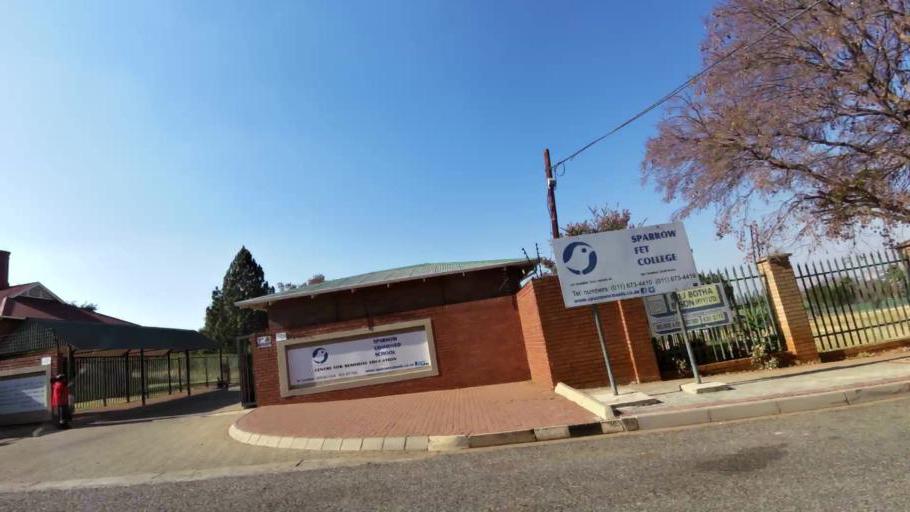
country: ZA
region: Gauteng
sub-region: City of Johannesburg Metropolitan Municipality
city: Johannesburg
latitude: -26.1722
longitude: 27.9845
